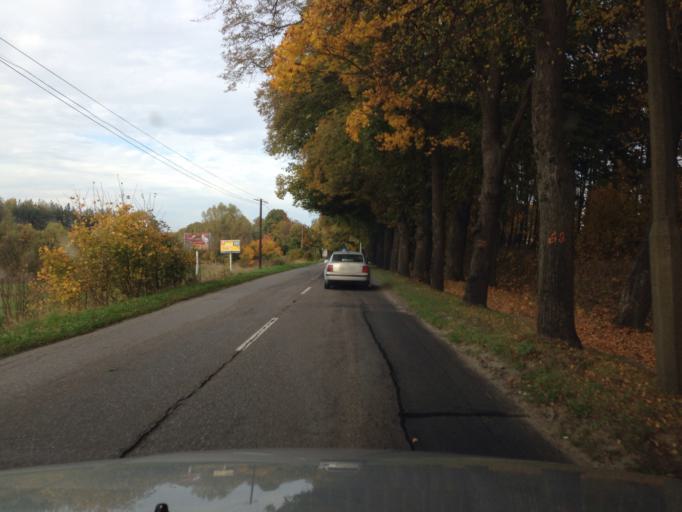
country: PL
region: Pomeranian Voivodeship
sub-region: Powiat koscierski
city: Koscierzyna
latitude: 54.1050
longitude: 17.9753
